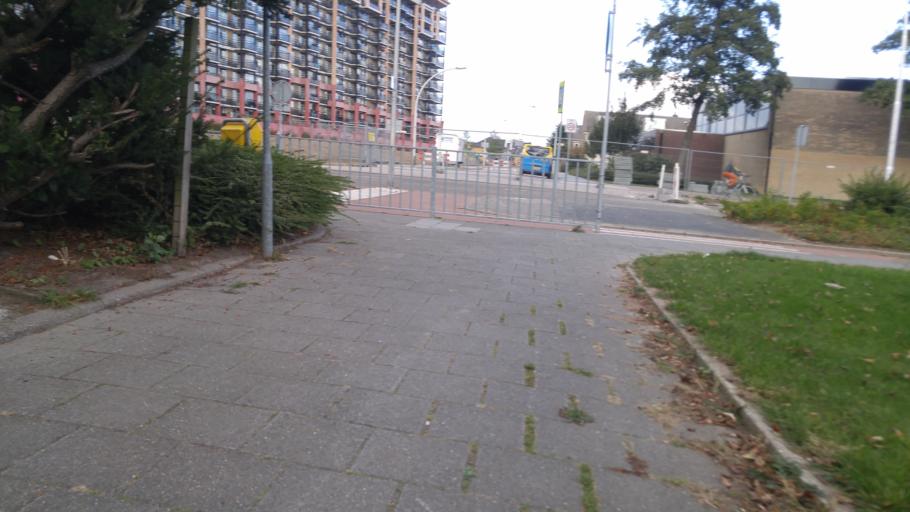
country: NL
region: South Holland
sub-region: Gemeente Zwijndrecht
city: Zwijndrecht
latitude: 51.8249
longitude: 4.6416
